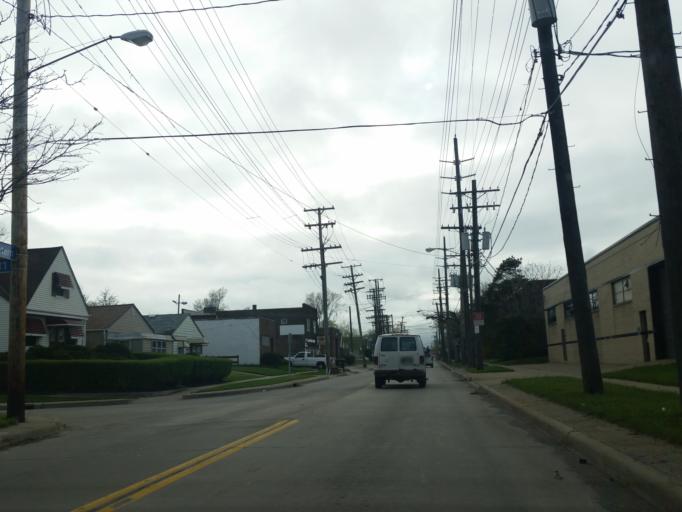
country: US
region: Ohio
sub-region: Cuyahoga County
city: Lakewood
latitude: 41.4704
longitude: -81.7636
